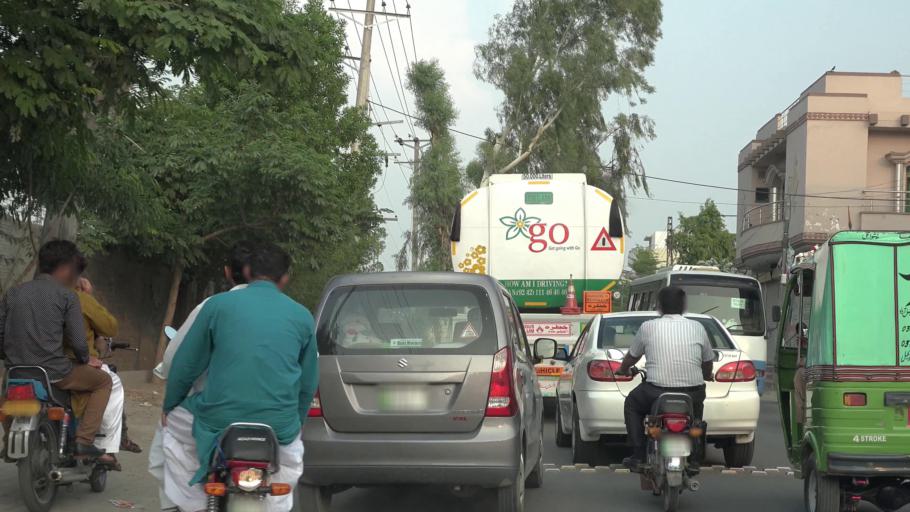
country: PK
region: Punjab
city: Faisalabad
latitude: 31.4456
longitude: 73.1288
